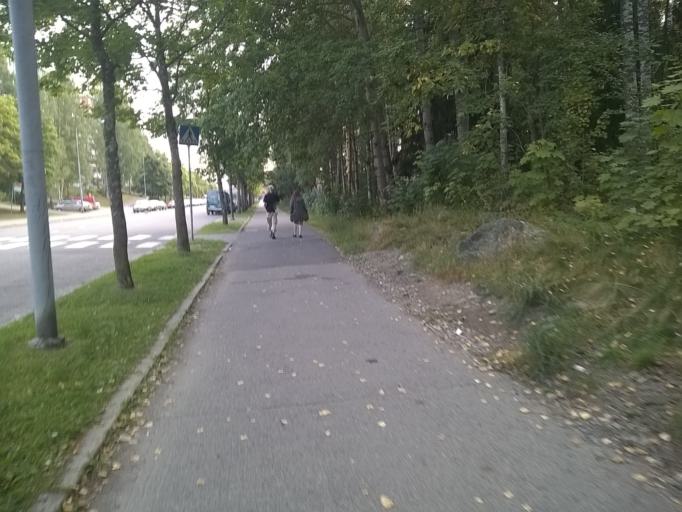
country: FI
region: Pirkanmaa
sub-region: Tampere
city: Tampere
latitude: 61.4494
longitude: 23.8434
